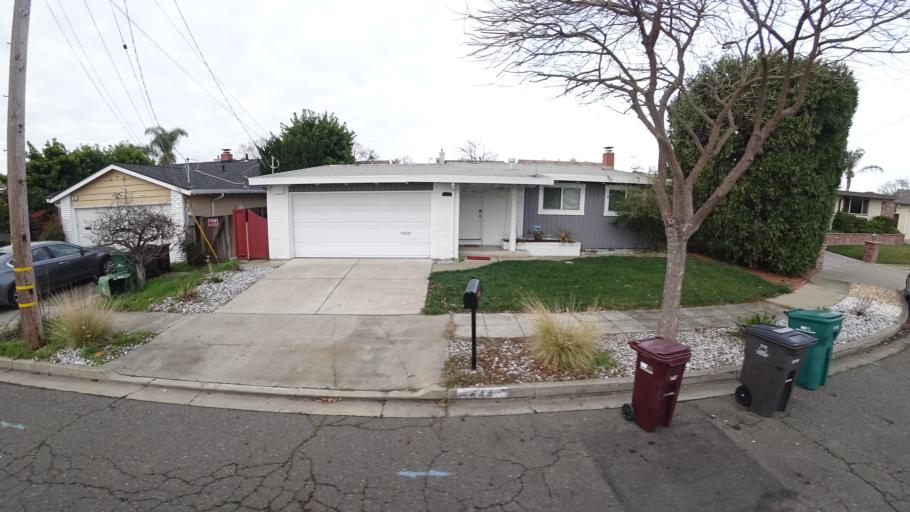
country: US
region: California
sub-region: Alameda County
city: Union City
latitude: 37.6232
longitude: -122.0423
